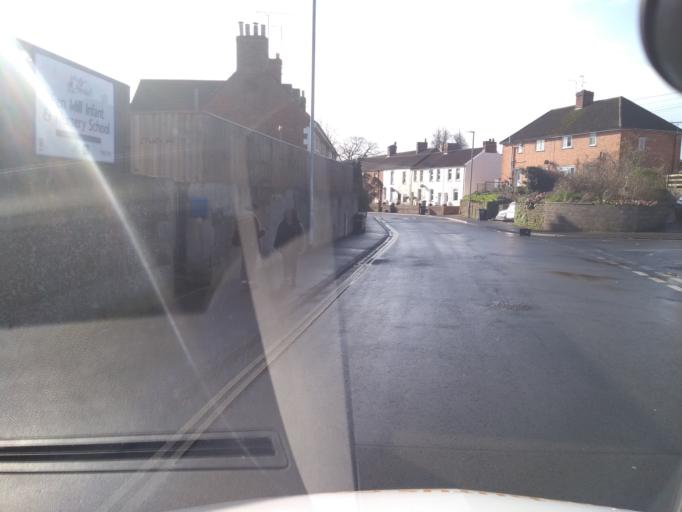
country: GB
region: England
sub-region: Somerset
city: Yeovil
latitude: 50.9462
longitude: -2.6200
